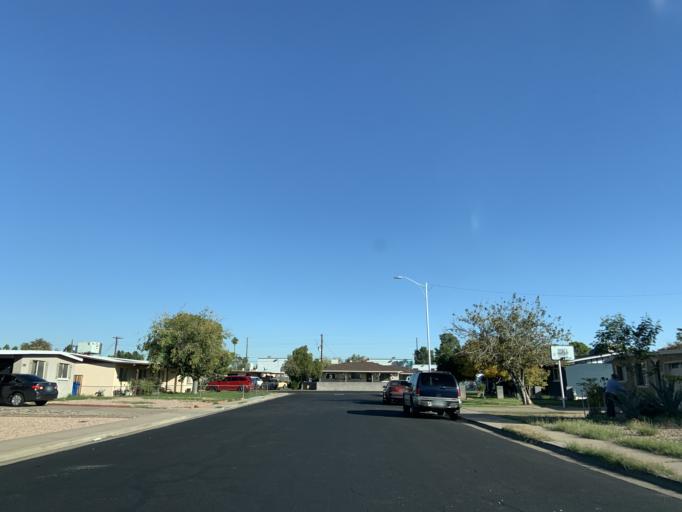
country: US
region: Arizona
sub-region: Maricopa County
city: Mesa
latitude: 33.4022
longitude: -111.8595
